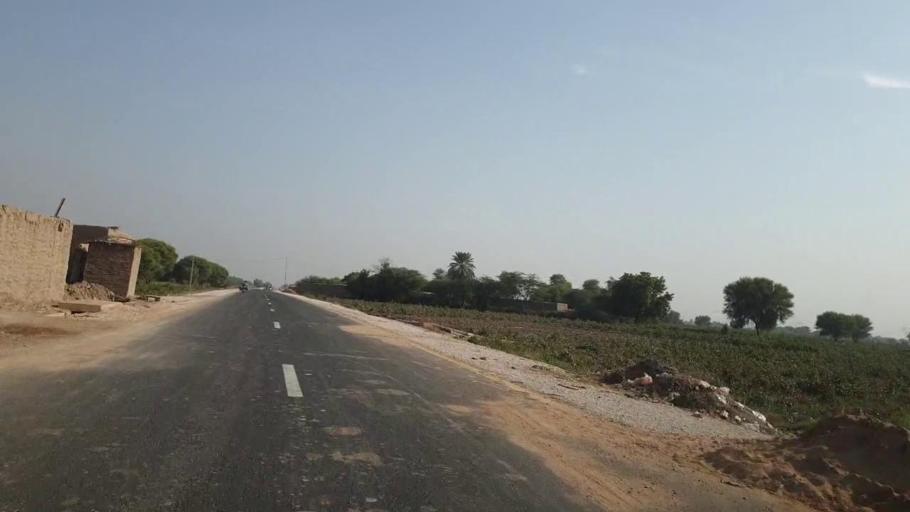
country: PK
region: Sindh
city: Sehwan
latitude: 26.4801
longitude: 67.7824
